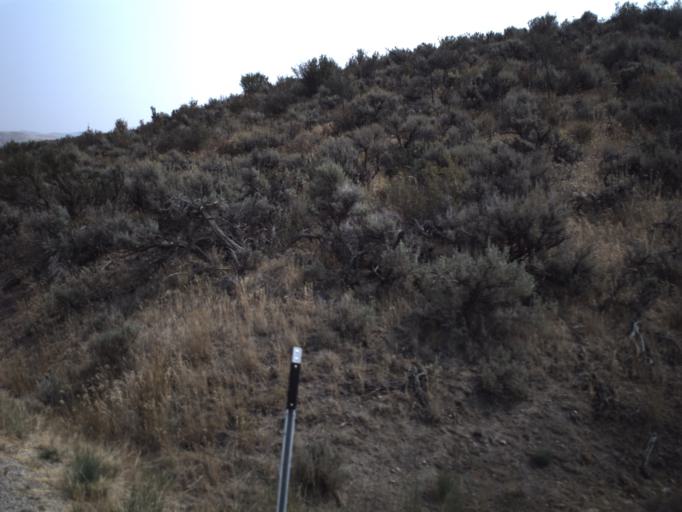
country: US
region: Utah
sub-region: Summit County
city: Coalville
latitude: 40.9717
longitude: -111.5396
